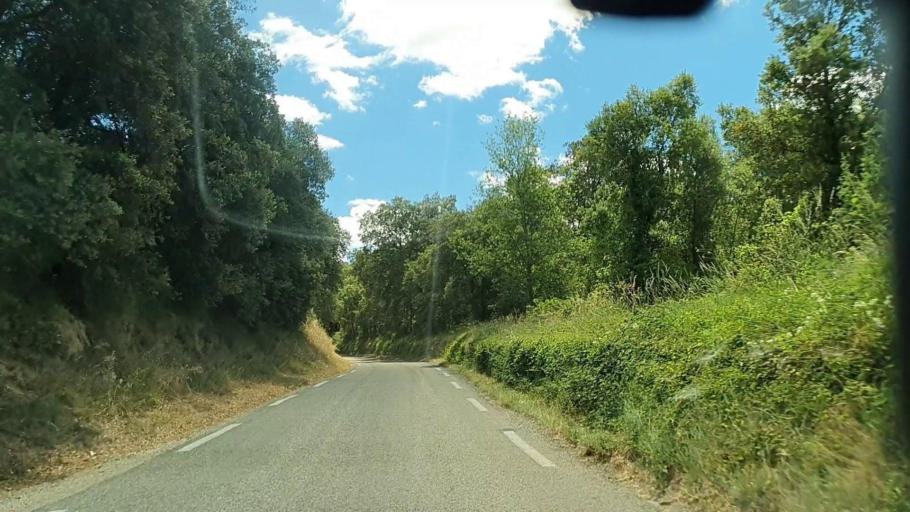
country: FR
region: Languedoc-Roussillon
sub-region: Departement du Gard
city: Cabrieres
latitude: 43.9097
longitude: 4.4624
